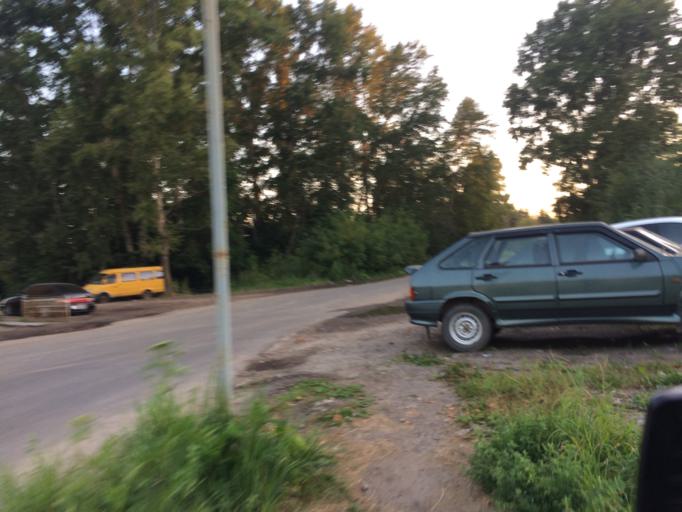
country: RU
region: Mariy-El
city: Yoshkar-Ola
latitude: 56.6428
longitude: 47.9132
